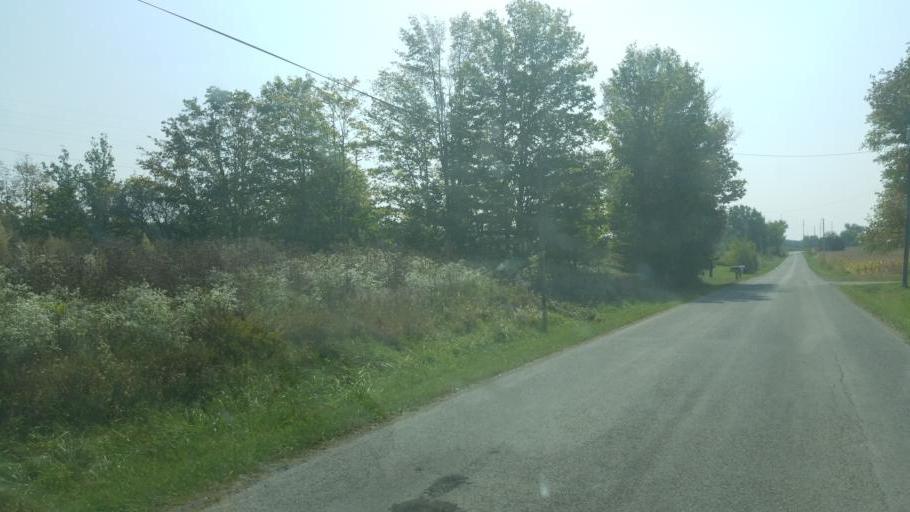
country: US
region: Ohio
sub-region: Morrow County
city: Mount Gilead
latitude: 40.6203
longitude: -82.8420
